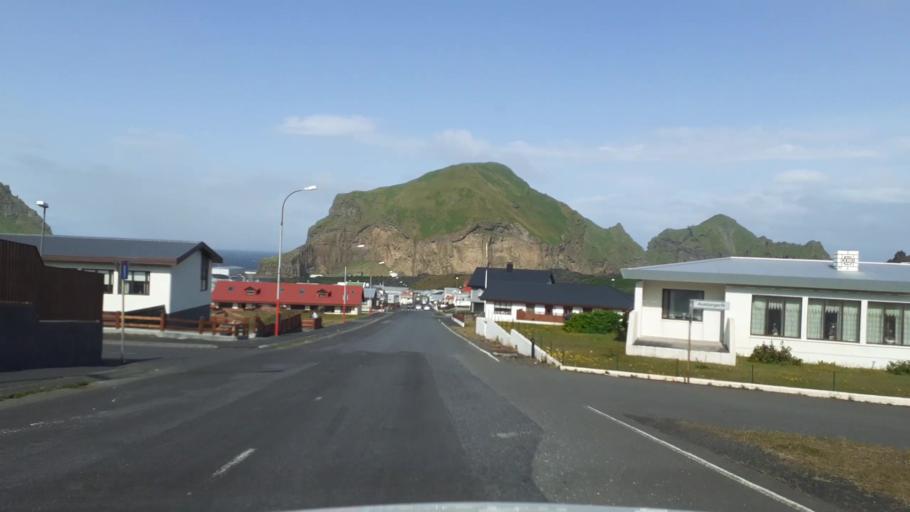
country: IS
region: South
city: Vestmannaeyjar
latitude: 63.4347
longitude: -20.2627
